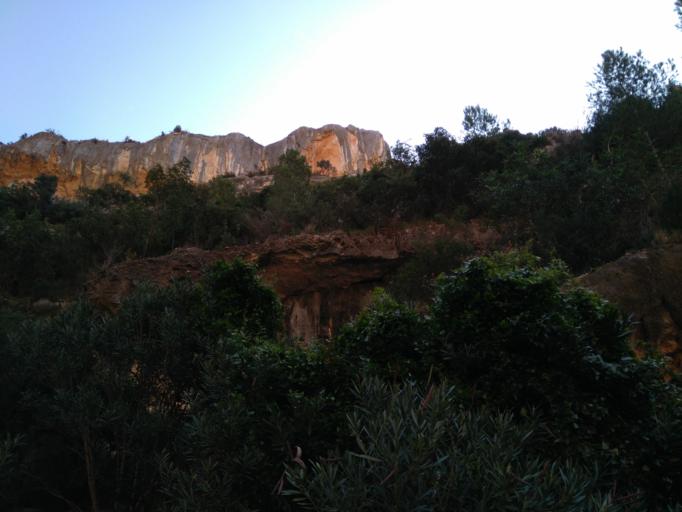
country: ES
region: Valencia
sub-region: Provincia de Valencia
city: Sumacarcer
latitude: 39.1604
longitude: -0.6593
